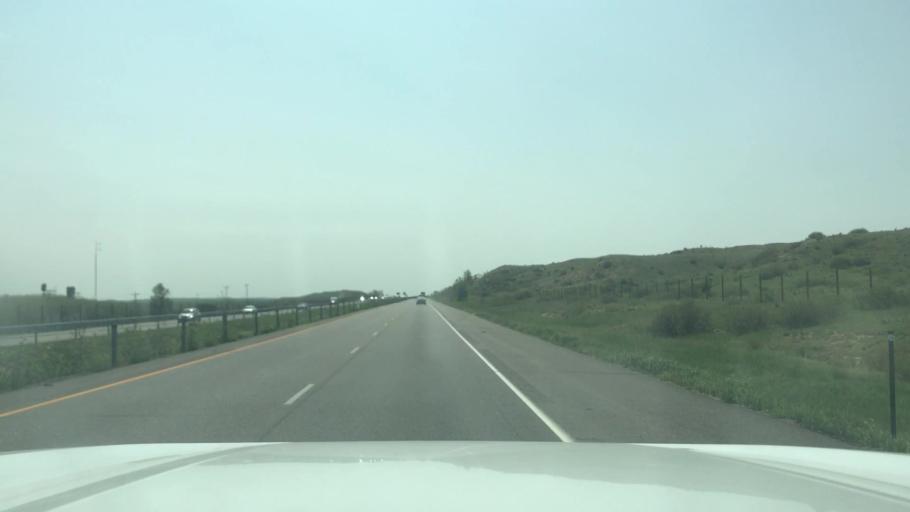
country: US
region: Colorado
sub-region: El Paso County
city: Fountain
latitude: 38.6534
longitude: -104.6978
